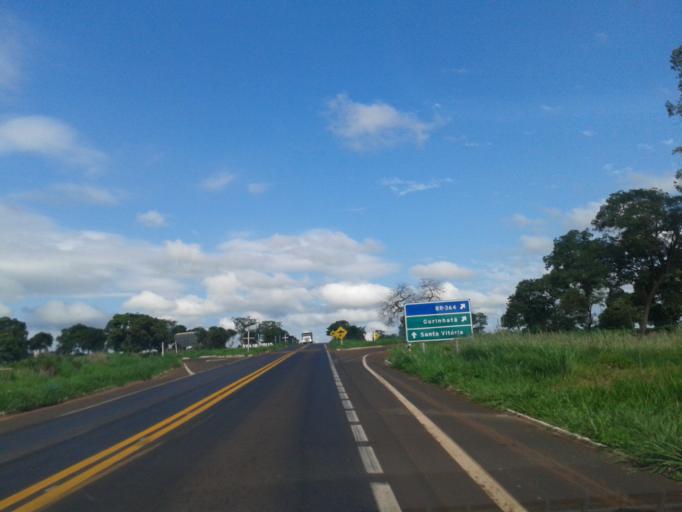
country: BR
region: Minas Gerais
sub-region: Santa Vitoria
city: Santa Vitoria
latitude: -18.9368
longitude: -49.8230
